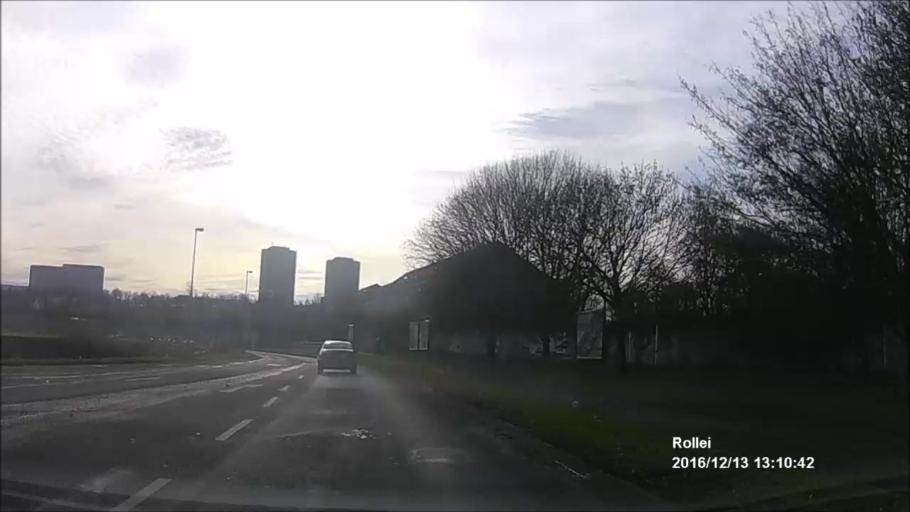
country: DE
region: Thuringia
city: Erfurt
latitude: 50.9688
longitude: 11.0605
